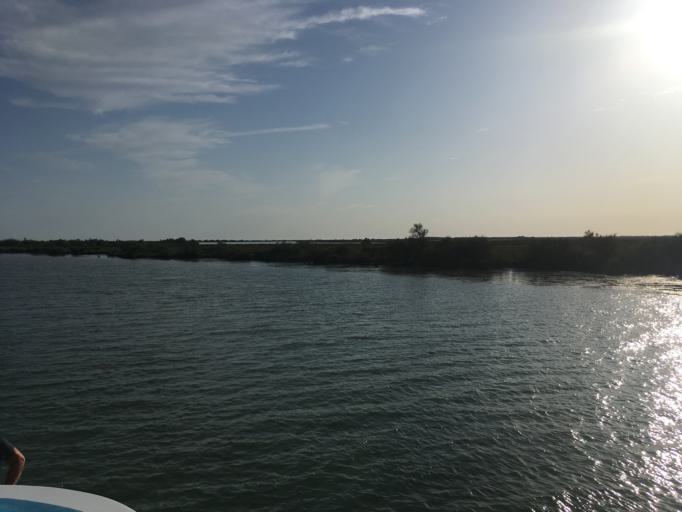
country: FR
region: Provence-Alpes-Cote d'Azur
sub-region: Departement des Bouches-du-Rhone
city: Saintes-Maries-de-la-Mer
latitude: 43.4619
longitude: 4.3903
